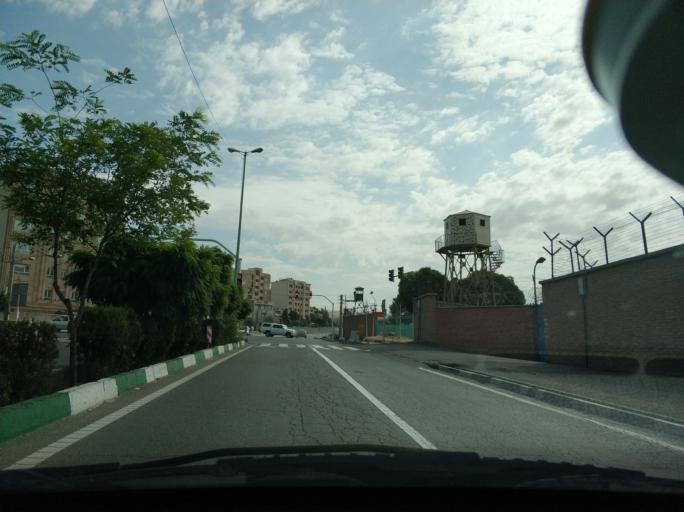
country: IR
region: Tehran
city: Tehran
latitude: 35.7315
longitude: 51.5951
